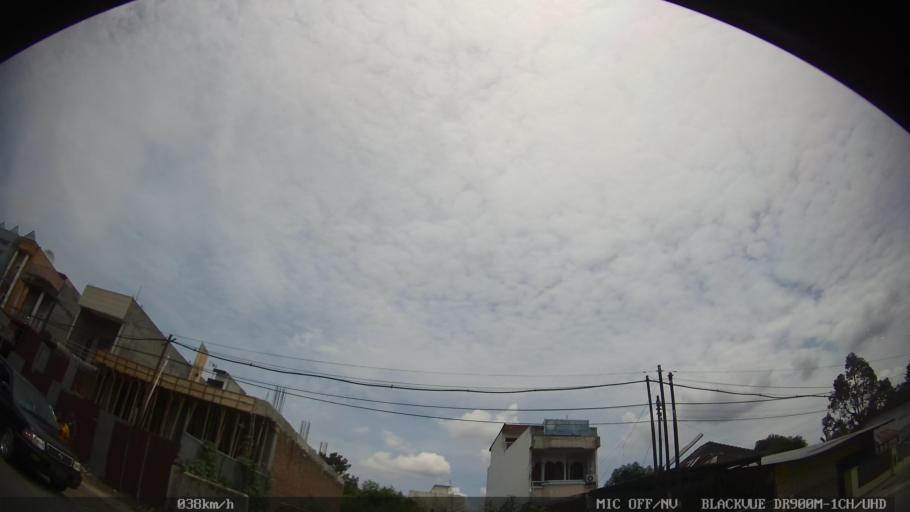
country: ID
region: North Sumatra
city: Sunggal
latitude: 3.5272
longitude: 98.6340
